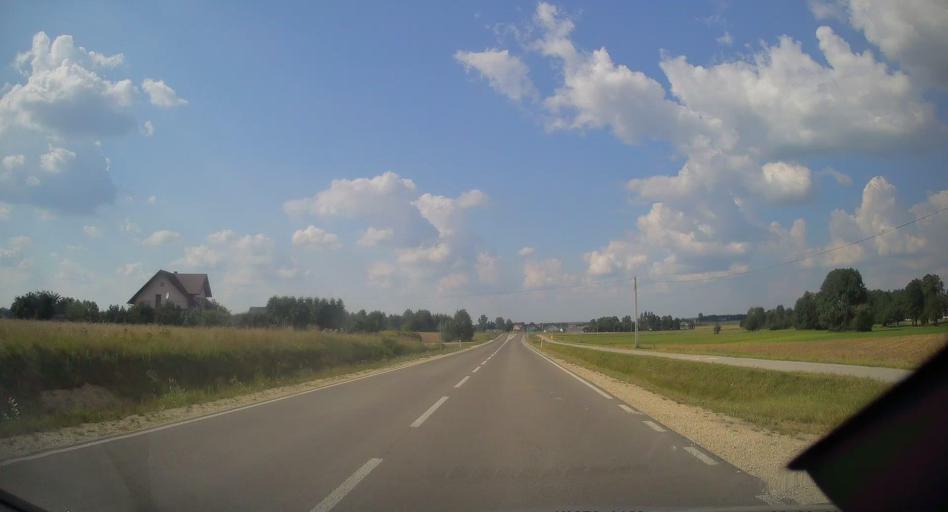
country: PL
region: Swietokrzyskie
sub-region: Powiat kielecki
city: Lopuszno
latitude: 50.9625
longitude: 20.2469
